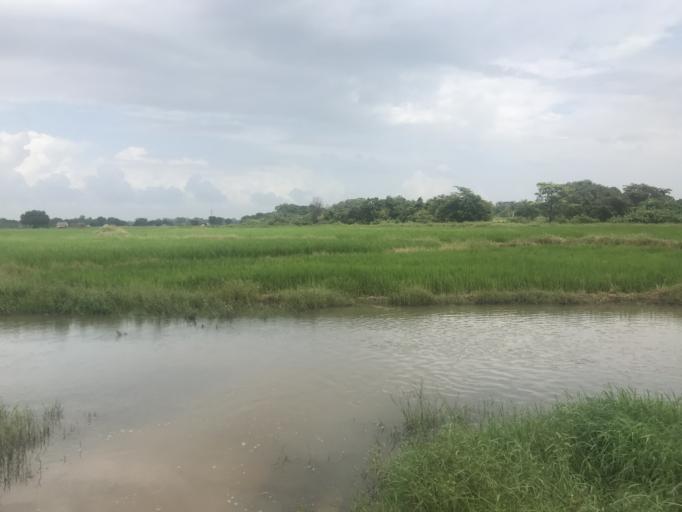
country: LK
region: Uva
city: Wattegama
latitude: 6.9585
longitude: 81.8007
